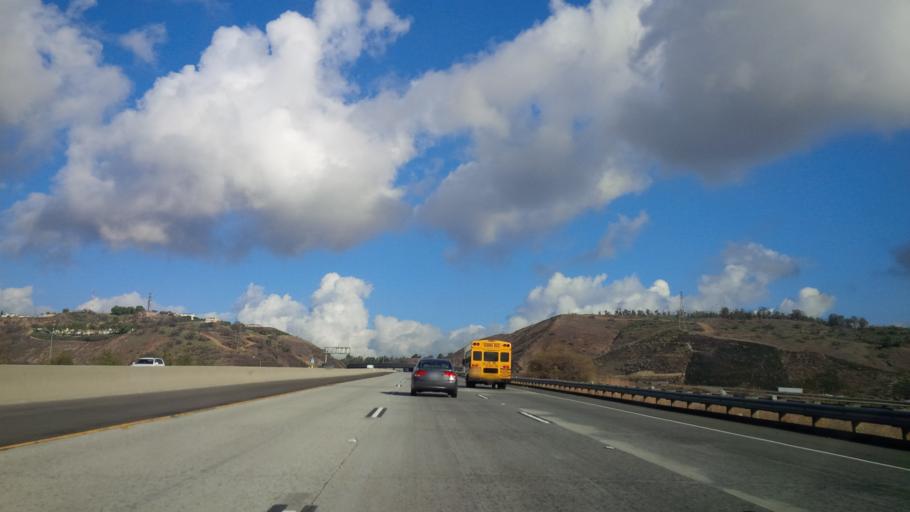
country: US
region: California
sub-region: Los Angeles County
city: Diamond Bar
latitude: 34.0623
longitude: -117.8055
